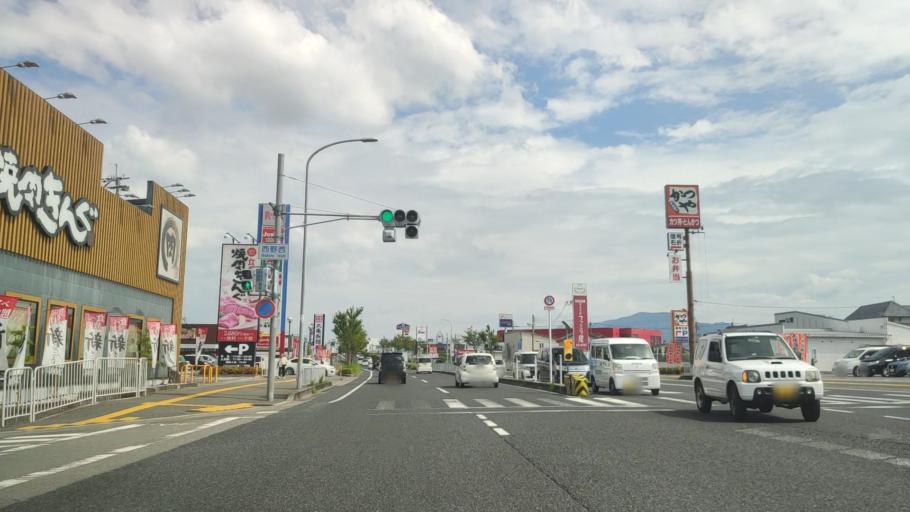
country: JP
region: Wakayama
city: Iwade
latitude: 34.2592
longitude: 135.3057
